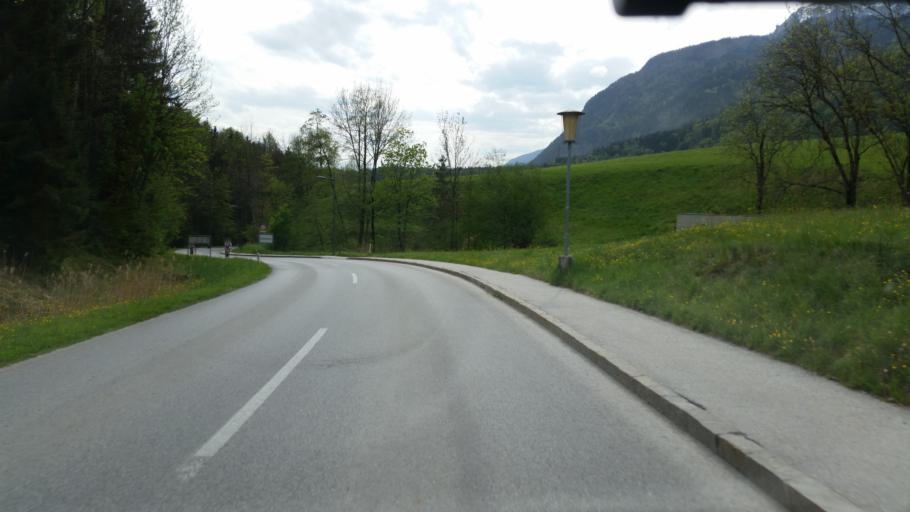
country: AT
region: Tyrol
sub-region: Politischer Bezirk Kufstein
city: Kramsach
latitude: 47.4534
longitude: 11.8787
